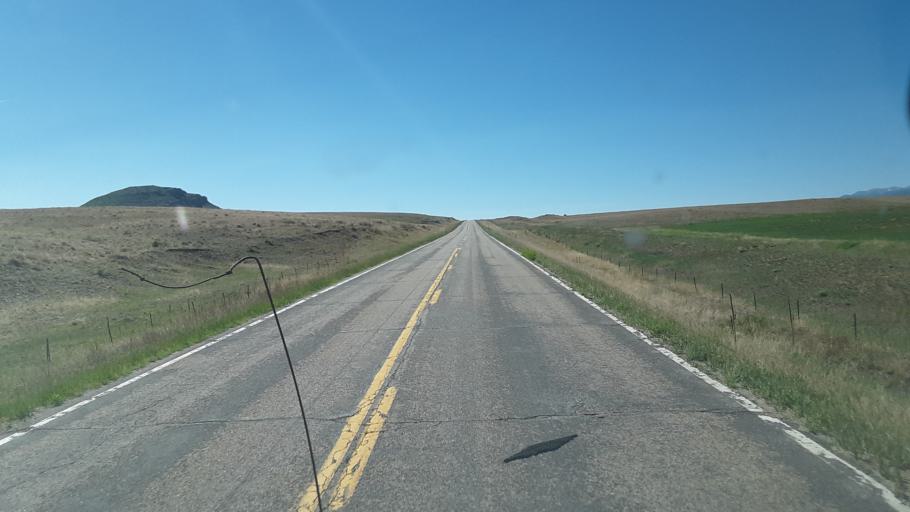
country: US
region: Colorado
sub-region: Custer County
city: Westcliffe
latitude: 38.2115
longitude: -105.5458
